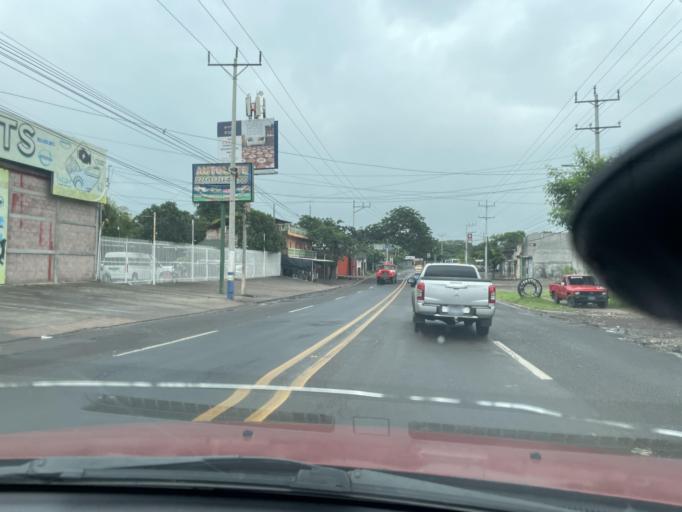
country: SV
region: San Miguel
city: San Miguel
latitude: 13.4990
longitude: -88.1670
